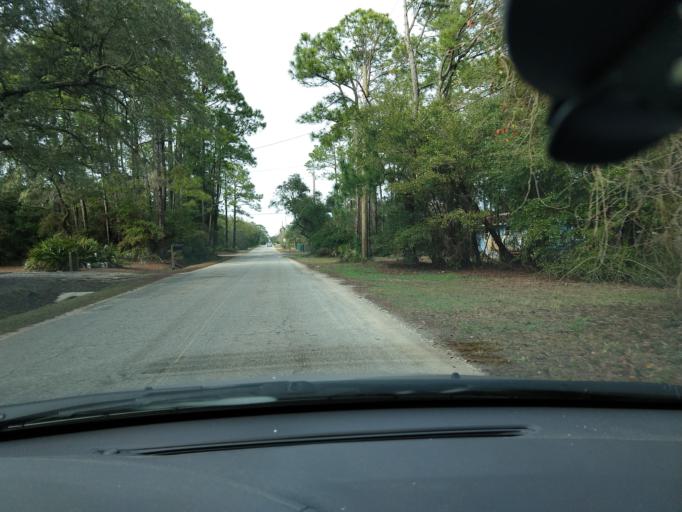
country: US
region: Florida
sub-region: Santa Rosa County
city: Woodlawn Beach
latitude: 30.3889
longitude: -86.9967
